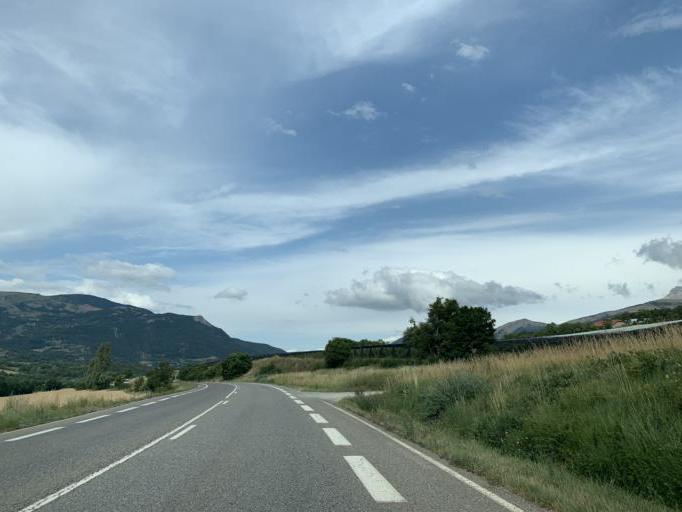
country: FR
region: Provence-Alpes-Cote d'Azur
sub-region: Departement des Hautes-Alpes
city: La Roche-des-Arnauds
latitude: 44.5465
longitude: 5.9986
